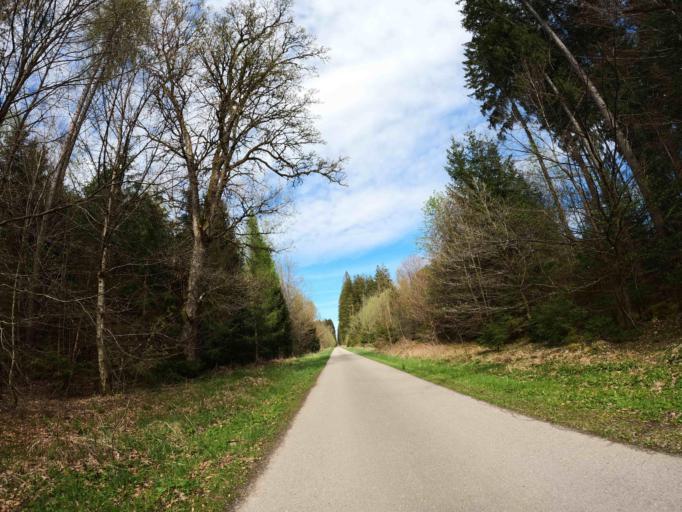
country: DE
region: Bavaria
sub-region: Upper Bavaria
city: Strasslach-Dingharting
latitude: 48.0186
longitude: 11.5306
